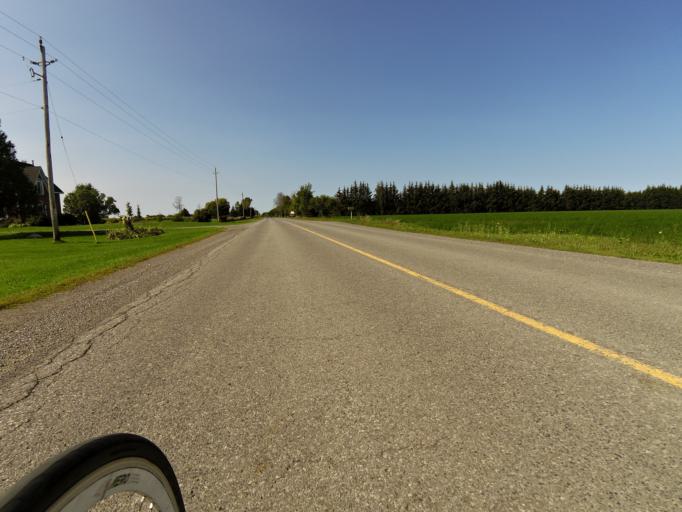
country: CA
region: Ontario
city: Carleton Place
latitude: 45.3489
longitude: -76.1108
